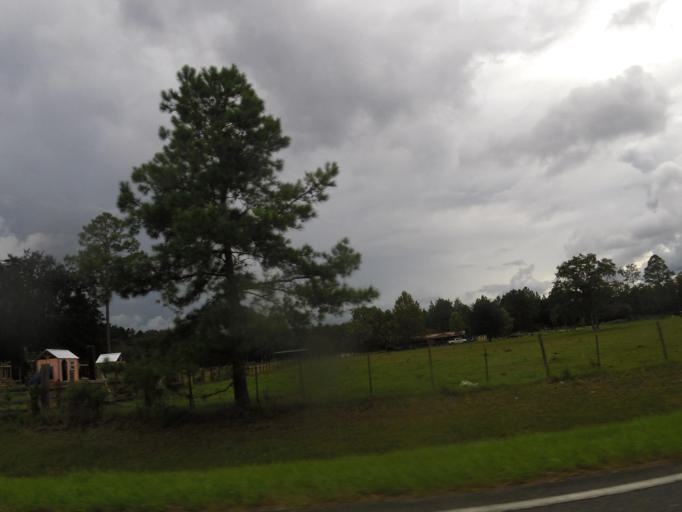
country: US
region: Florida
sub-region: Baker County
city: Macclenny
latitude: 30.4655
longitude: -82.1989
